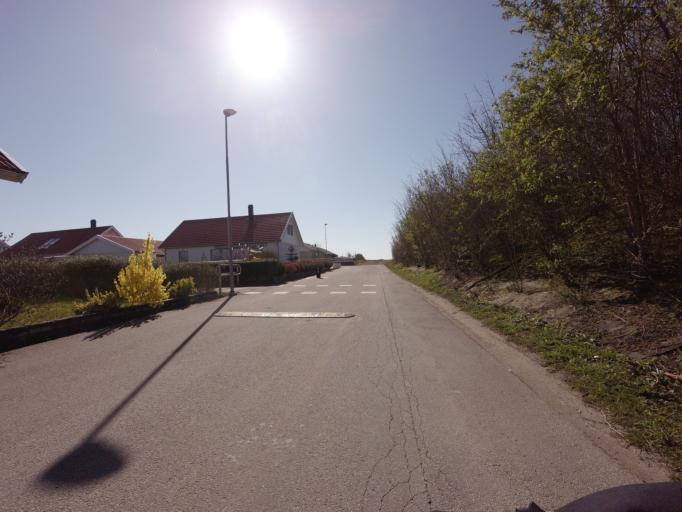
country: SE
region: Skane
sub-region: Malmo
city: Oxie
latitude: 55.4629
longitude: 13.1366
